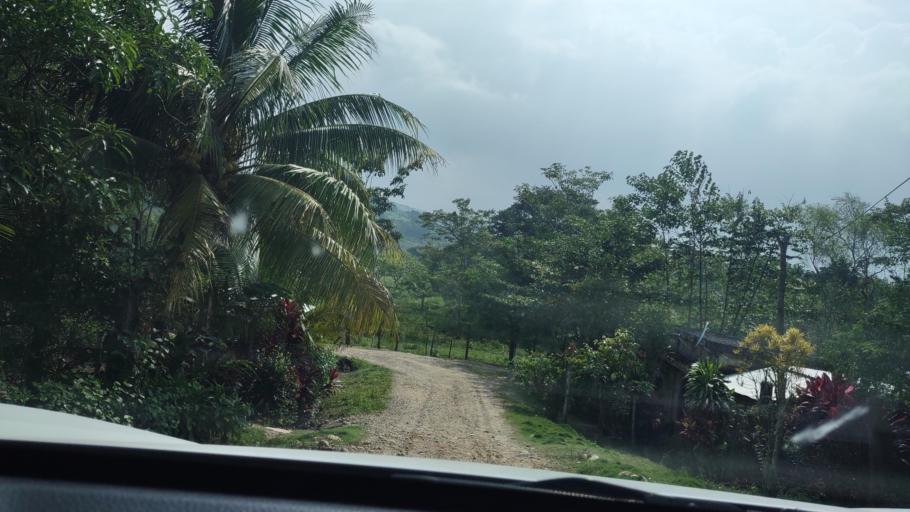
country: MX
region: Veracruz
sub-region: Uxpanapa
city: Poblado 10
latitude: 17.5456
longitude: -94.2917
